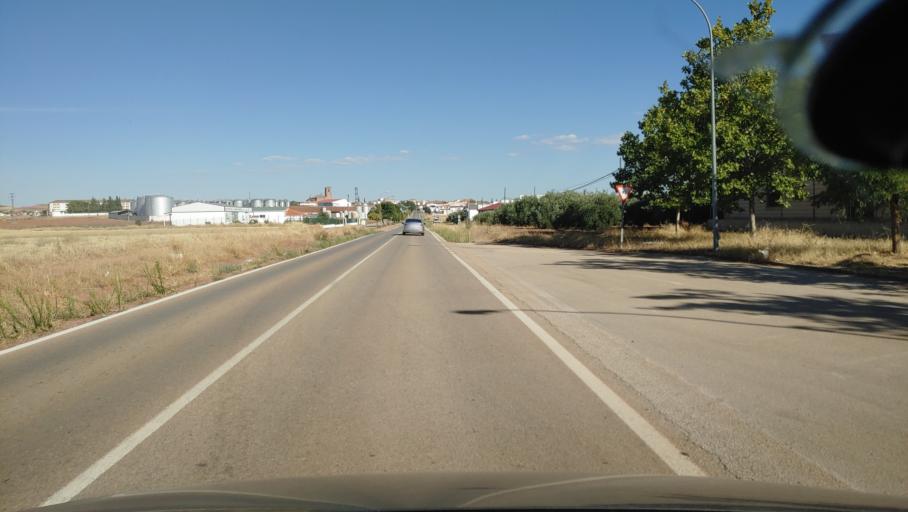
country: ES
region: Castille-La Mancha
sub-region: Provincia de Ciudad Real
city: Infantes
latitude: 38.7391
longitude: -3.0279
